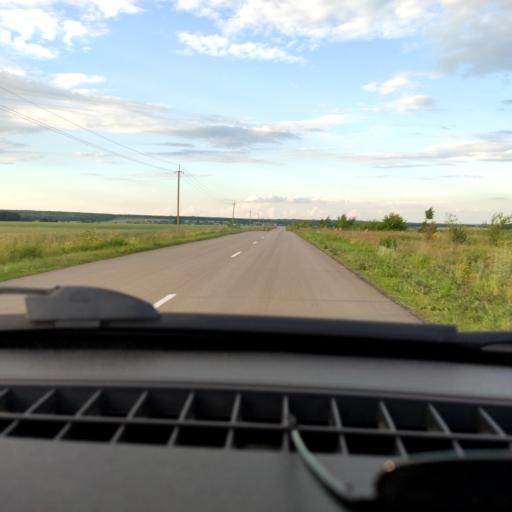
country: RU
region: Bashkortostan
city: Chishmy
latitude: 54.3811
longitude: 55.4325
